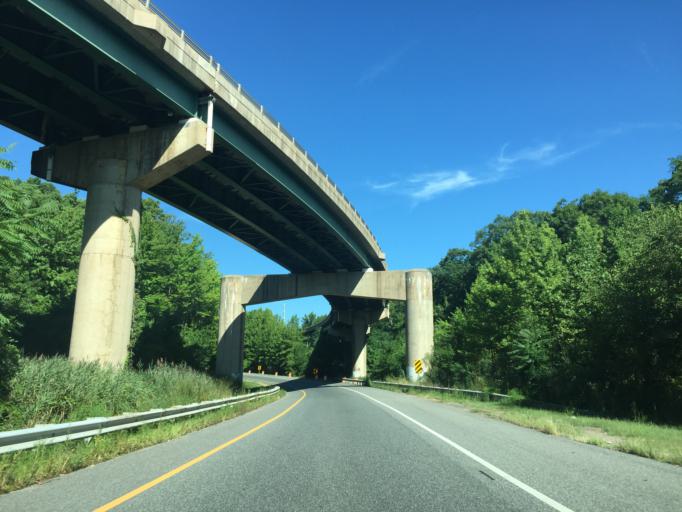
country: US
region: Maryland
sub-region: Baltimore County
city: Rossville
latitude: 39.3249
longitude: -76.4777
